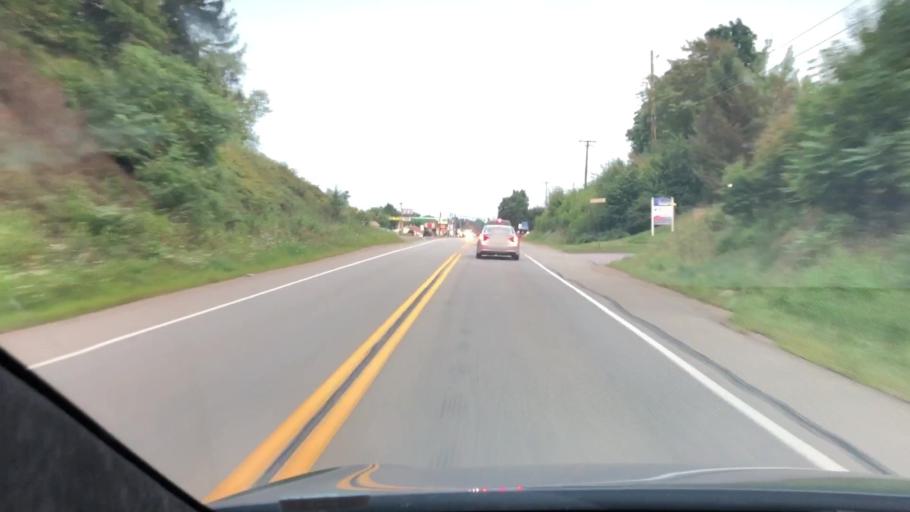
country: US
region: Pennsylvania
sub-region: Butler County
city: Shanor-Northvue
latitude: 40.9110
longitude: -79.9324
